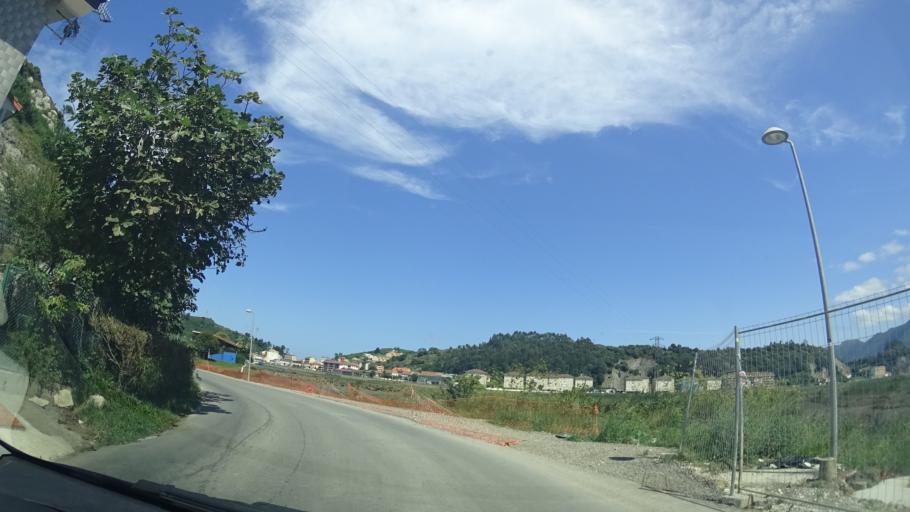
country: ES
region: Asturias
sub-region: Province of Asturias
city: Ribadesella
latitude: 43.4565
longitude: -5.0678
